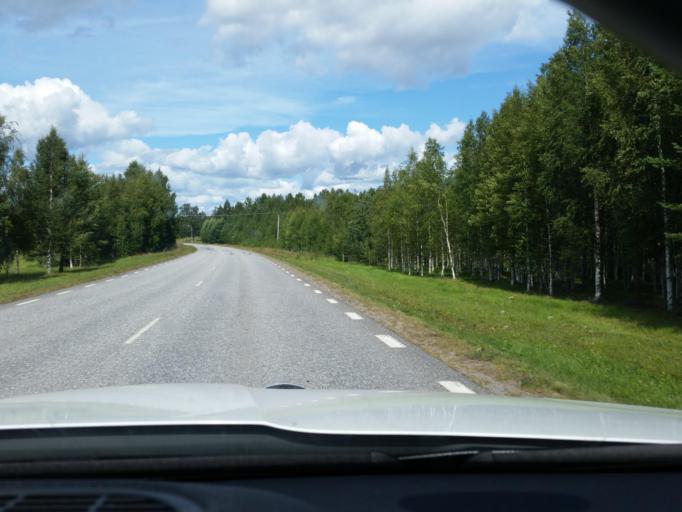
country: SE
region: Norrbotten
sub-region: Pitea Kommun
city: Norrfjarden
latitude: 65.4286
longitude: 21.4923
